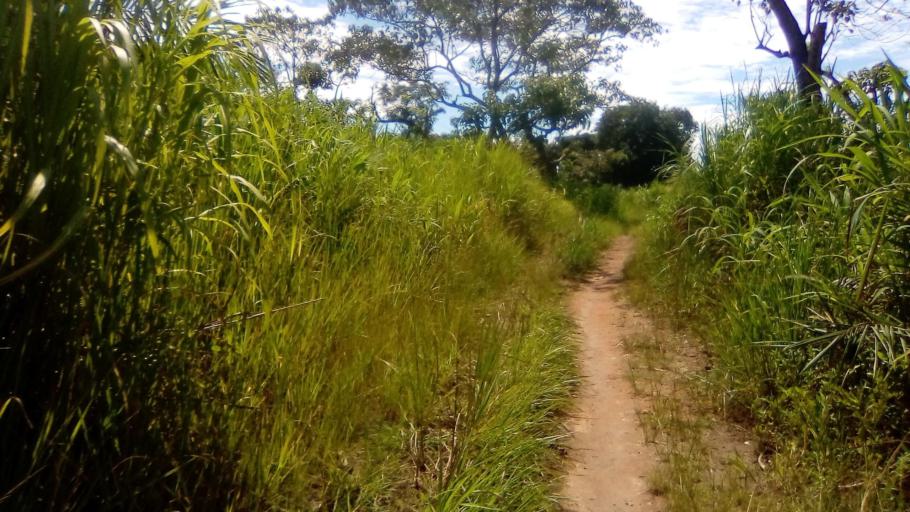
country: SL
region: Eastern Province
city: Simbakoro
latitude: 8.6317
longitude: -11.0014
